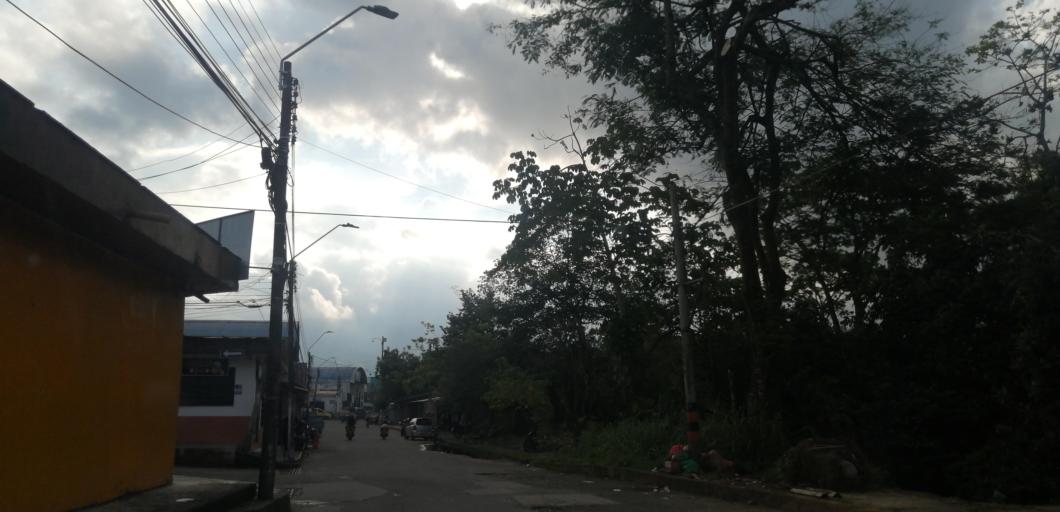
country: CO
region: Meta
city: Acacias
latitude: 3.9886
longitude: -73.7610
